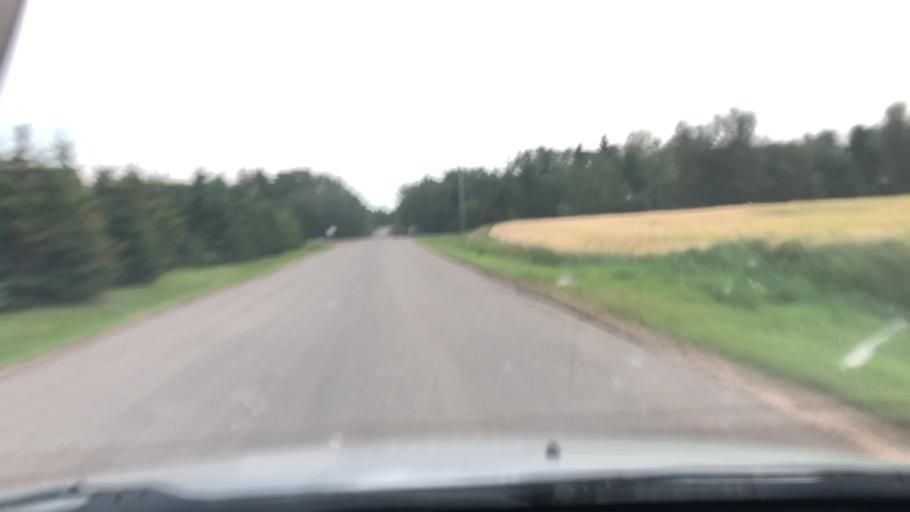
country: CA
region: Alberta
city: Devon
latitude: 53.4297
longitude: -113.6769
